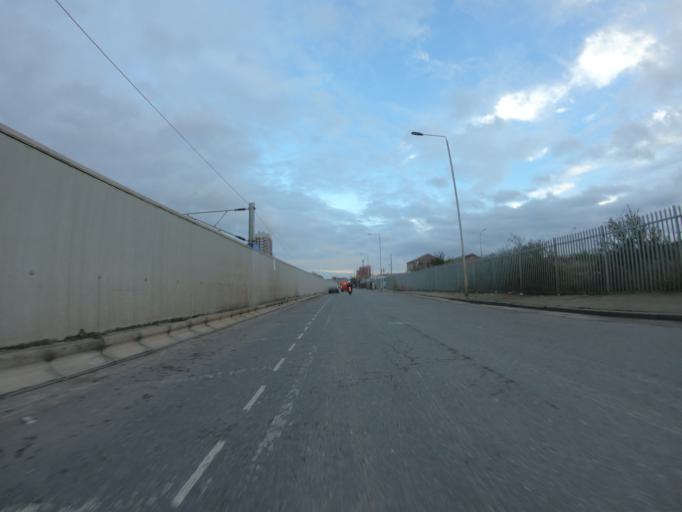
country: GB
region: England
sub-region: Greater London
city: Woolwich
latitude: 51.5009
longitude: 0.0538
